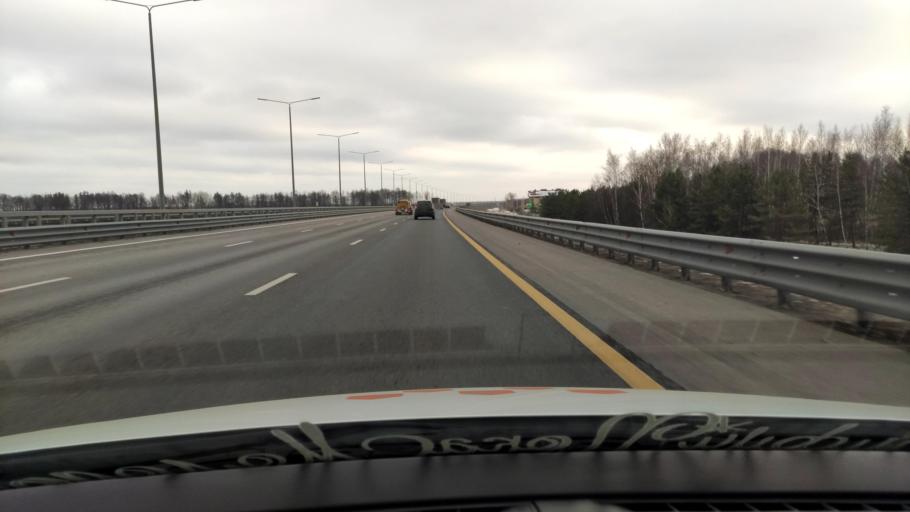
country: RU
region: Voronezj
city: Somovo
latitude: 51.7831
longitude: 39.2897
